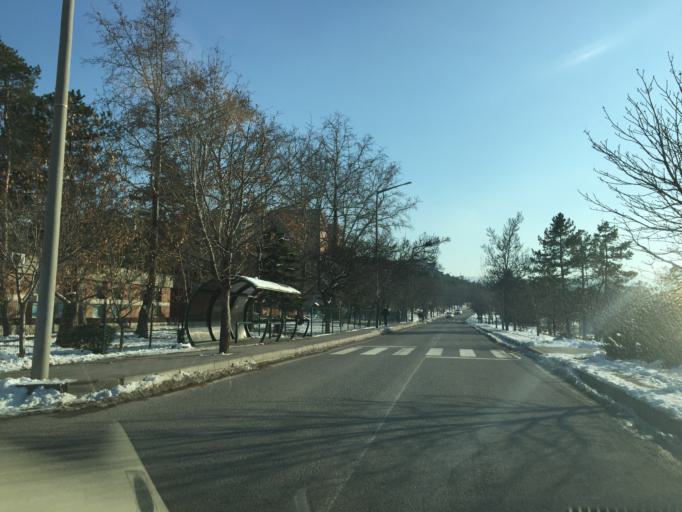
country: TR
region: Ankara
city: Ankara
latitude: 39.8959
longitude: 32.7807
